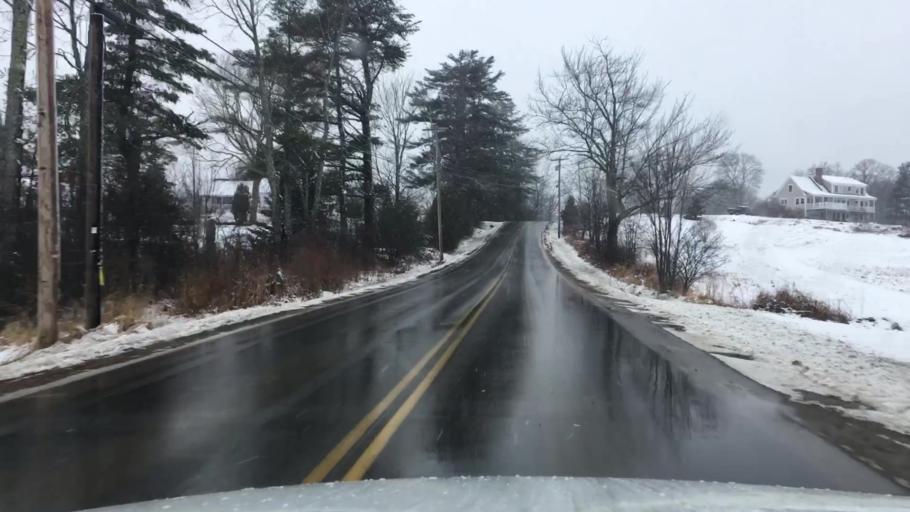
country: US
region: Maine
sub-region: Knox County
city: Warren
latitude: 44.1268
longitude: -69.2547
